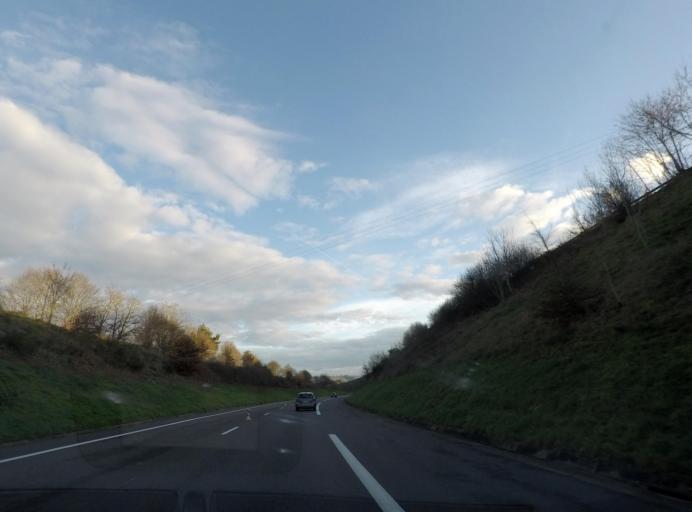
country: FR
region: Bourgogne
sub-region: Departement de Saone-et-Loire
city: Matour
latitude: 46.3803
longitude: 4.5263
